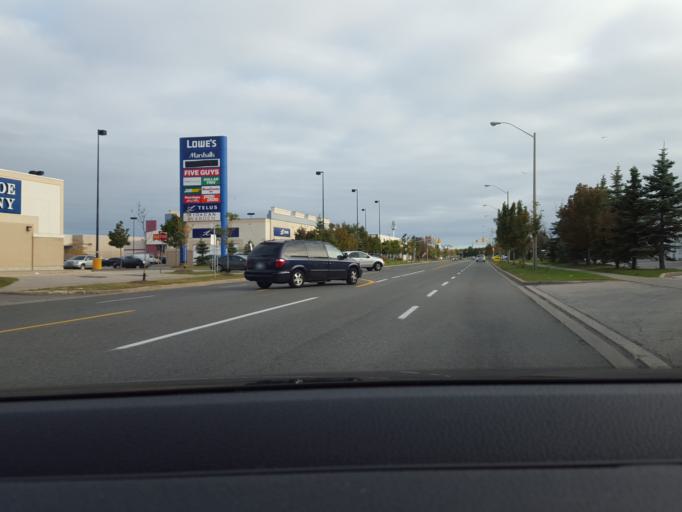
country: CA
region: Ontario
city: Scarborough
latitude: 43.7258
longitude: -79.2910
